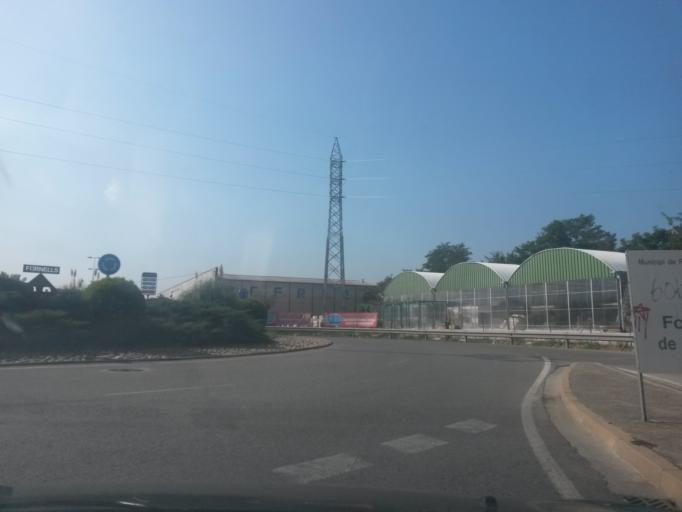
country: ES
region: Catalonia
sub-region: Provincia de Girona
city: Fornells de la Selva
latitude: 41.9492
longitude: 2.8059
